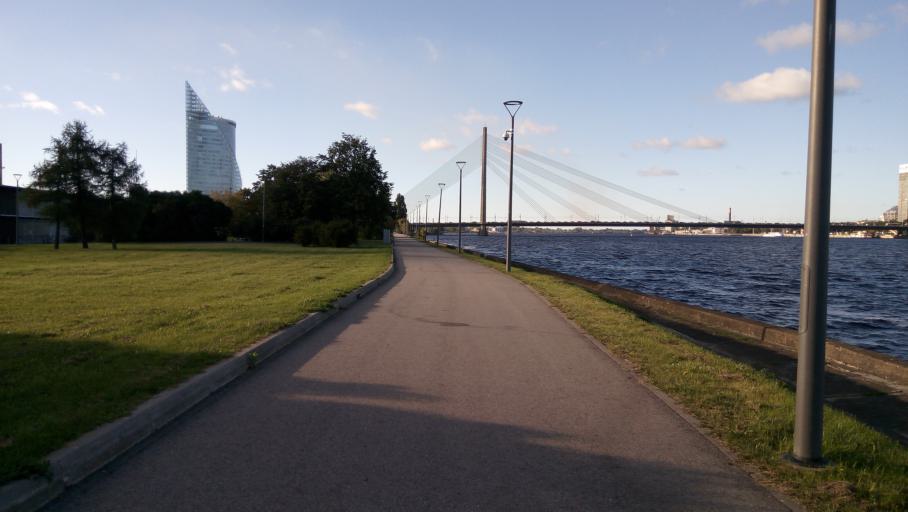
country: LV
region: Riga
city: Riga
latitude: 56.9448
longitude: 24.0965
